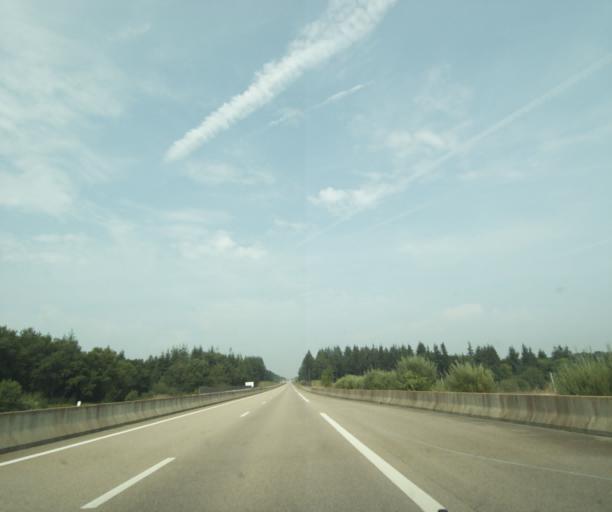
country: FR
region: Lower Normandy
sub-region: Departement de l'Orne
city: Courteilles
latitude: 48.8313
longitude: -0.1464
